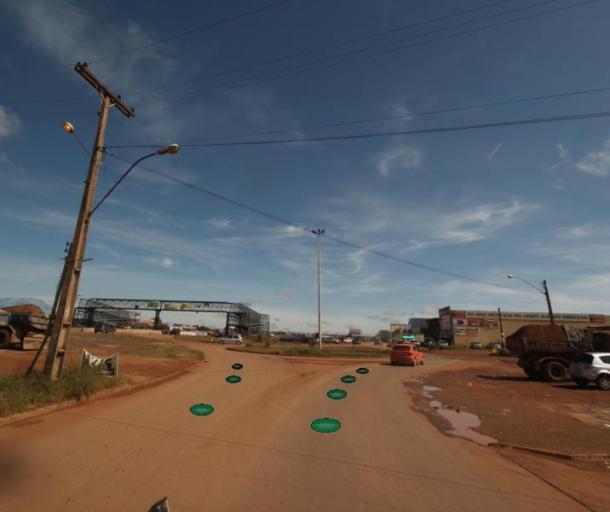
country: BR
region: Federal District
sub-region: Brasilia
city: Brasilia
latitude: -15.7515
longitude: -48.2598
